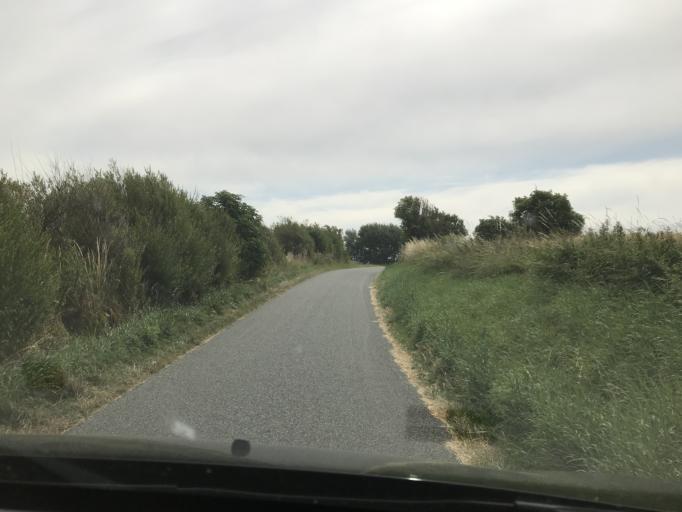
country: DK
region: South Denmark
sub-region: AEro Kommune
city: AEroskobing
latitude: 54.9217
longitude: 10.2483
